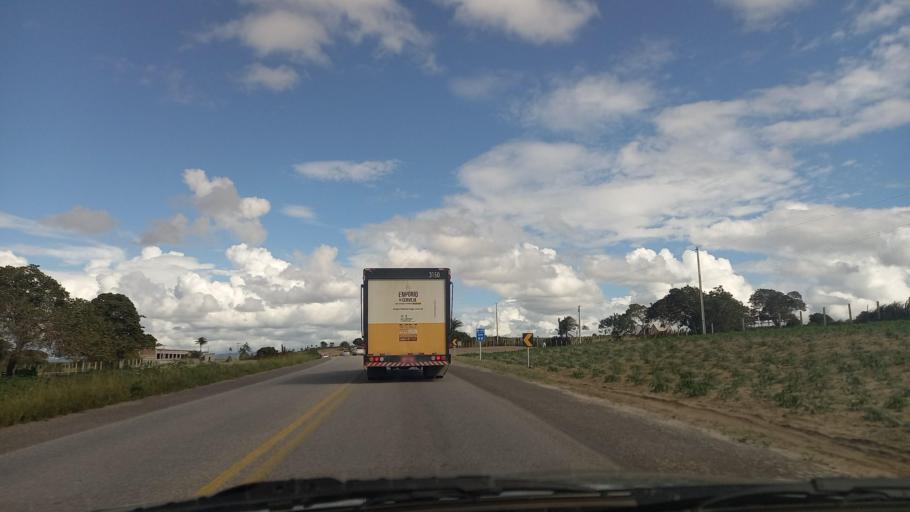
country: BR
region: Pernambuco
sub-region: Sao Joao
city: Sao Joao
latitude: -8.7624
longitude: -36.4302
